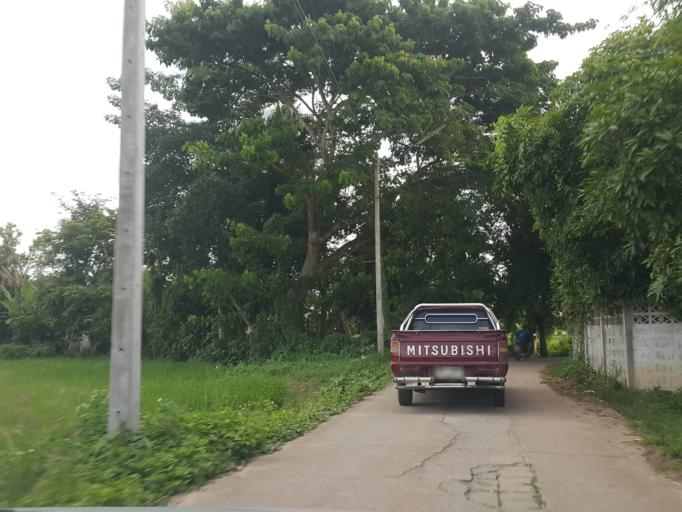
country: TH
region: Chiang Mai
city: San Sai
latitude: 18.8824
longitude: 99.0728
